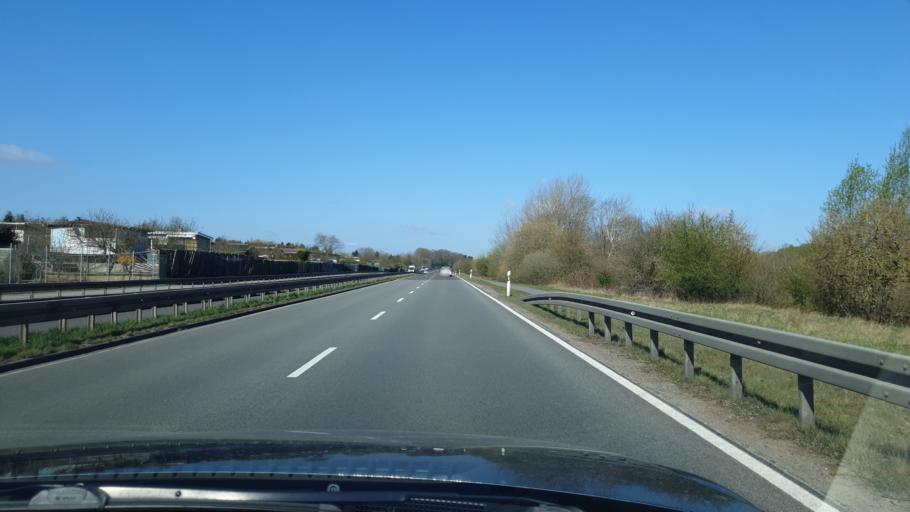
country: DE
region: Mecklenburg-Vorpommern
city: Neumuehle
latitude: 53.6179
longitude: 11.3769
